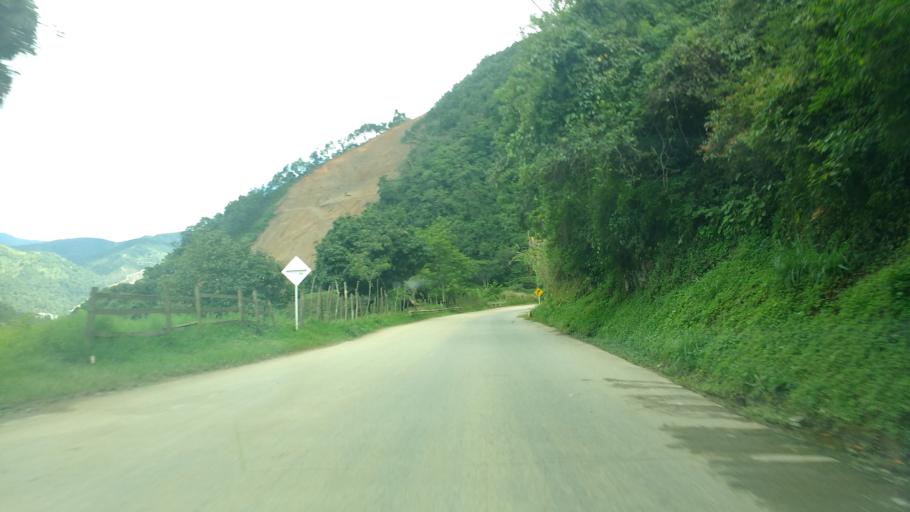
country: CO
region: Antioquia
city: Amaga
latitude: 6.0496
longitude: -75.7174
